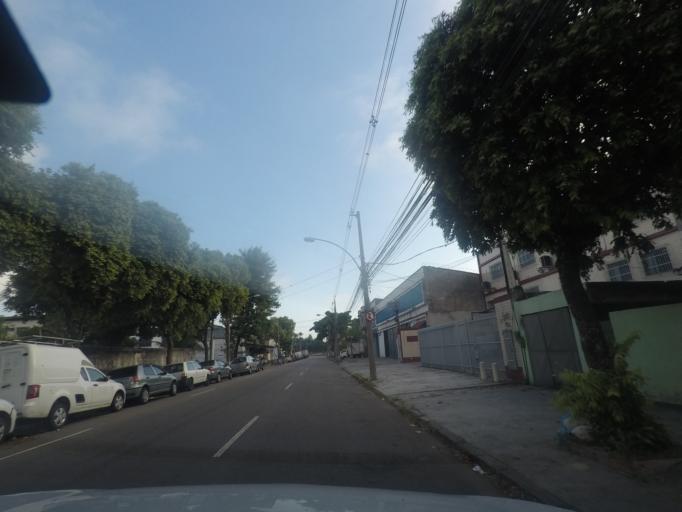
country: BR
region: Rio de Janeiro
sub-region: Duque De Caxias
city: Duque de Caxias
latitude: -22.8296
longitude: -43.2745
